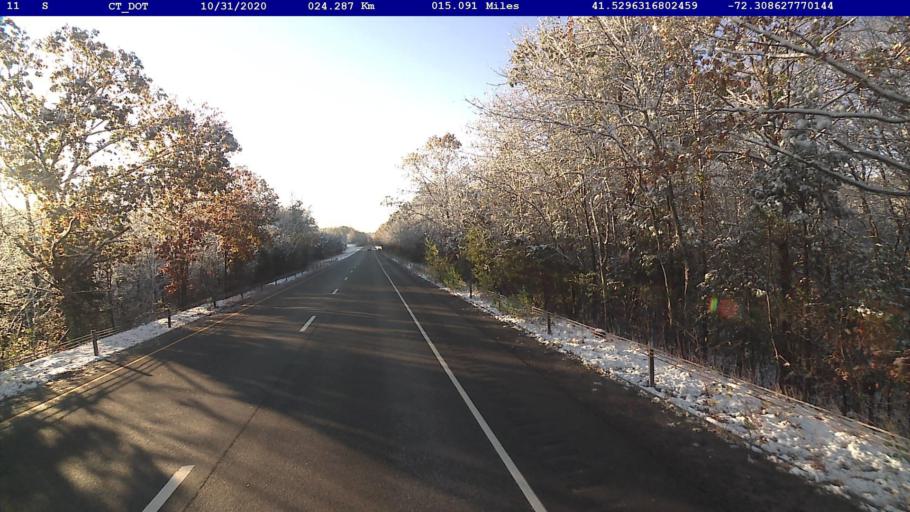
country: US
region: Connecticut
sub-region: New London County
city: Colchester
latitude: 41.5296
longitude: -72.3086
